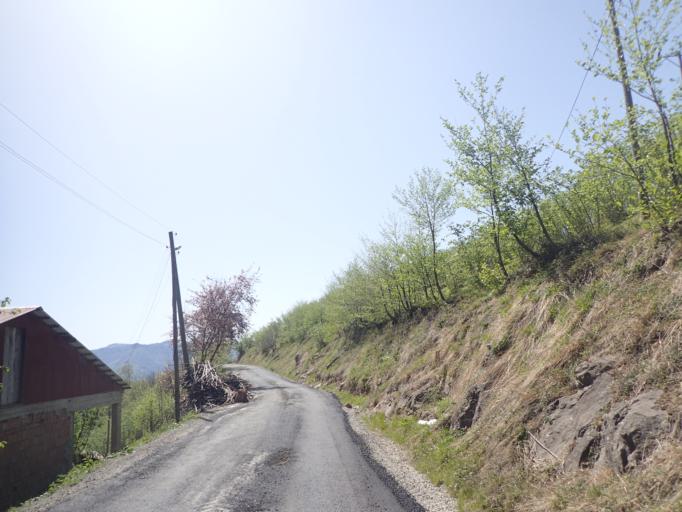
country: TR
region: Ordu
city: Kabaduz
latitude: 40.8038
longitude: 37.8962
